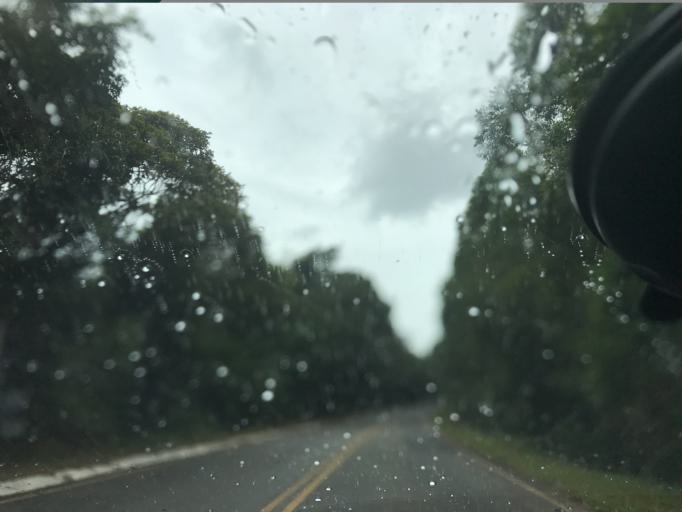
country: BR
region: Minas Gerais
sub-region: Conceicao Do Rio Verde
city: Conceicao do Rio Verde
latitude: -21.6804
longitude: -45.0175
